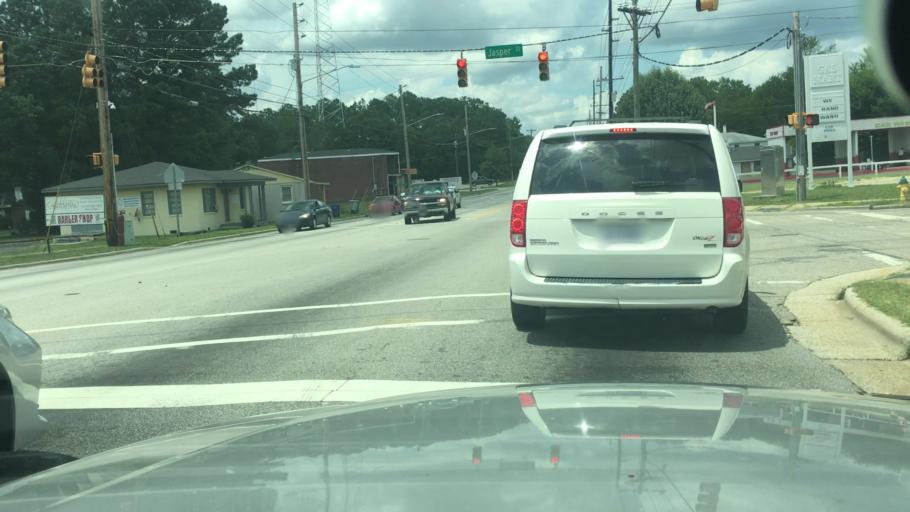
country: US
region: North Carolina
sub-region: Cumberland County
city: Fayetteville
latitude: 35.0845
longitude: -78.9047
